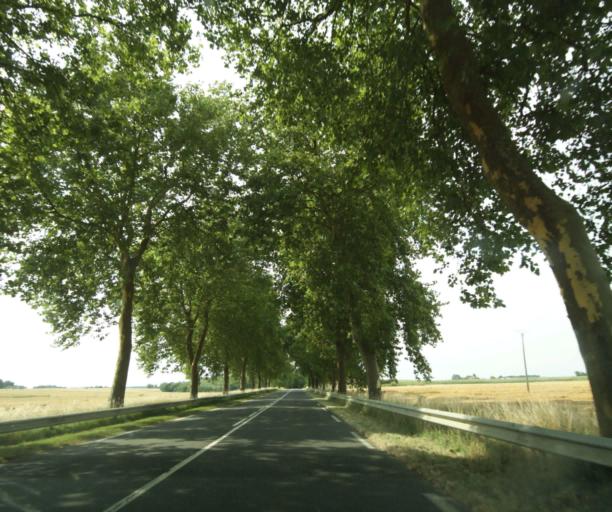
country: FR
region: Centre
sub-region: Departement d'Indre-et-Loire
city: Saint-Paterne-Racan
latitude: 47.6078
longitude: 0.5125
